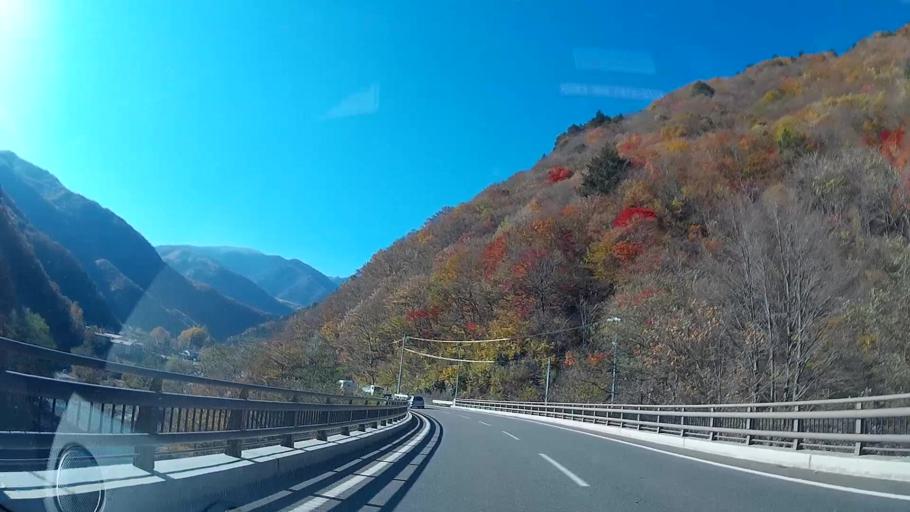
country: JP
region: Nagano
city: Toyoshina
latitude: 36.1648
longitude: 137.6653
